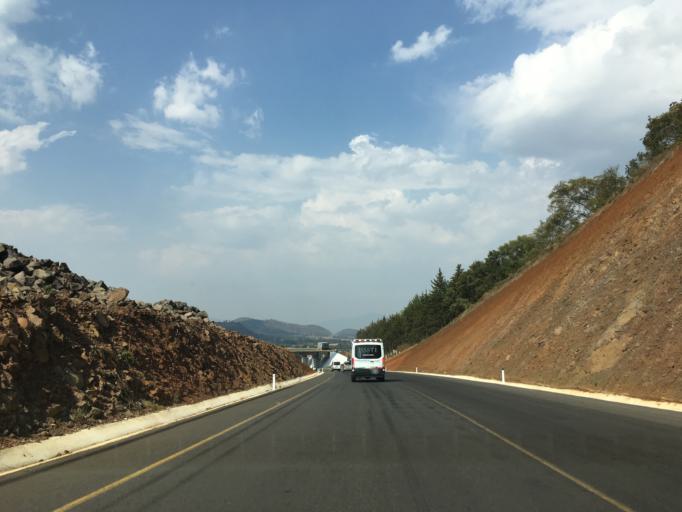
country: MX
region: Michoacan
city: Patzcuaro
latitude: 19.5250
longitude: -101.5682
